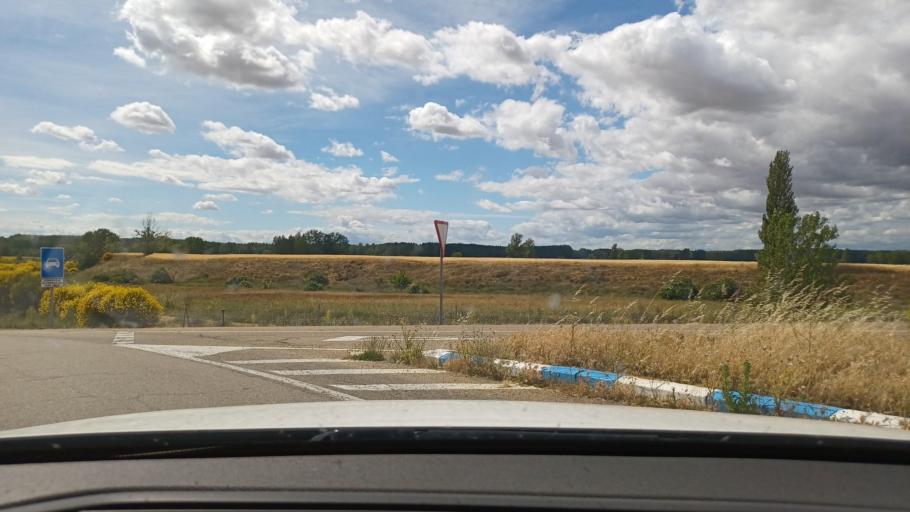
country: ES
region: Castille and Leon
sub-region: Provincia de Leon
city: Sahagun
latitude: 42.3847
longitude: -5.0274
